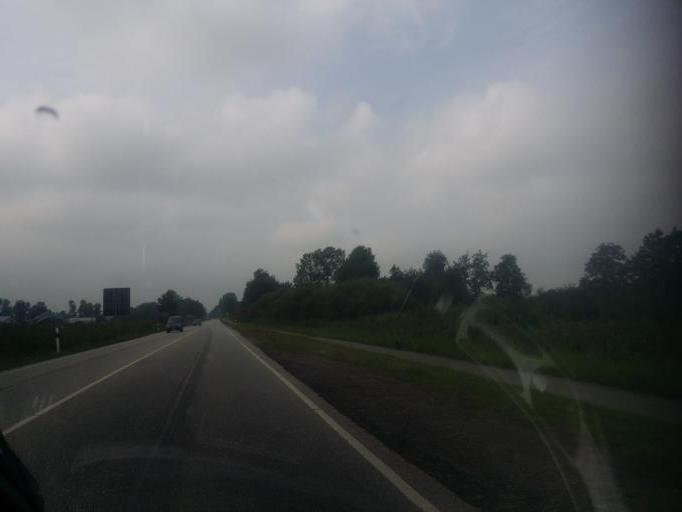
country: DE
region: Schleswig-Holstein
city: Koldenbuttel
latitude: 54.3795
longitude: 9.0723
